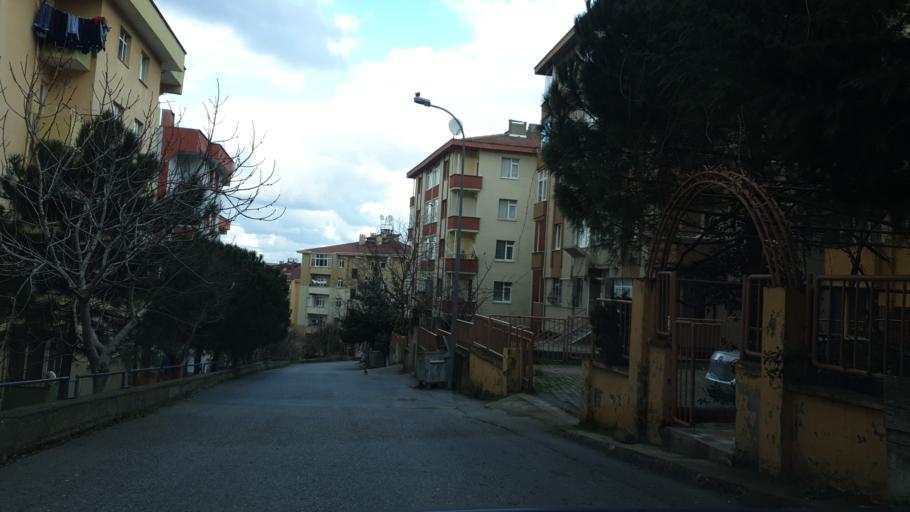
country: TR
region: Istanbul
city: Pendik
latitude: 40.9054
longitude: 29.2475
